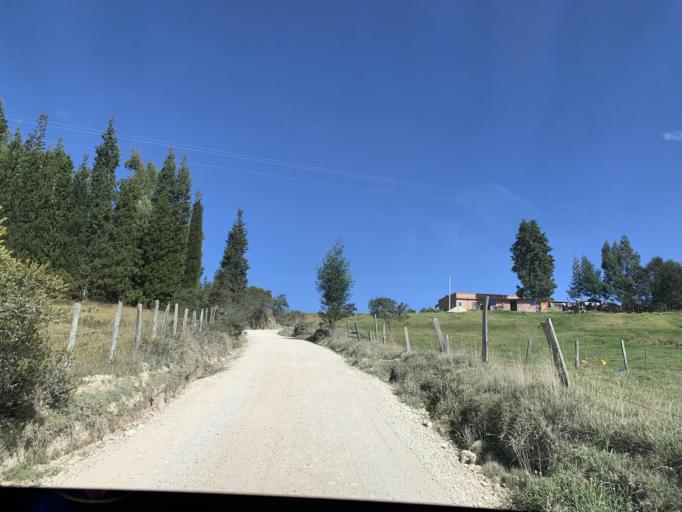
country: CO
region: Boyaca
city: Tuta
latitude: 5.7015
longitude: -73.1494
